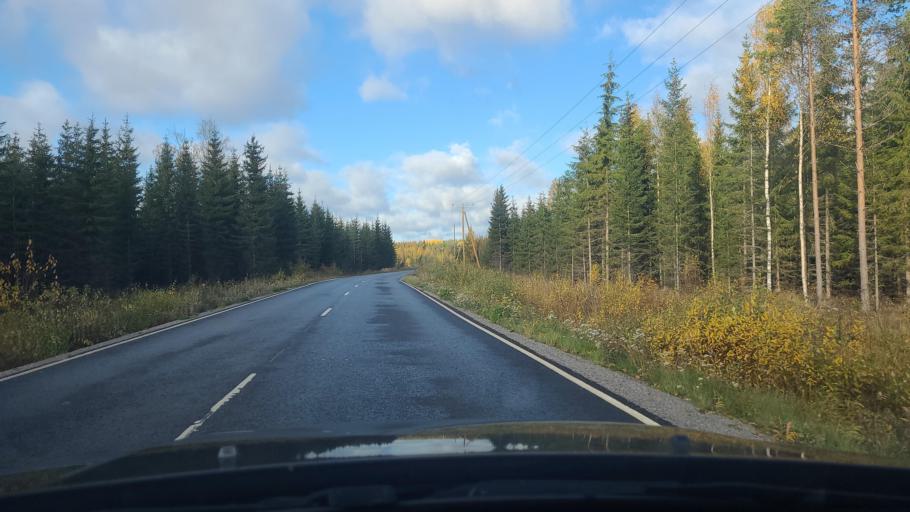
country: FI
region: Southern Savonia
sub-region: Pieksaemaeki
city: Juva
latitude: 61.8803
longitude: 27.7611
